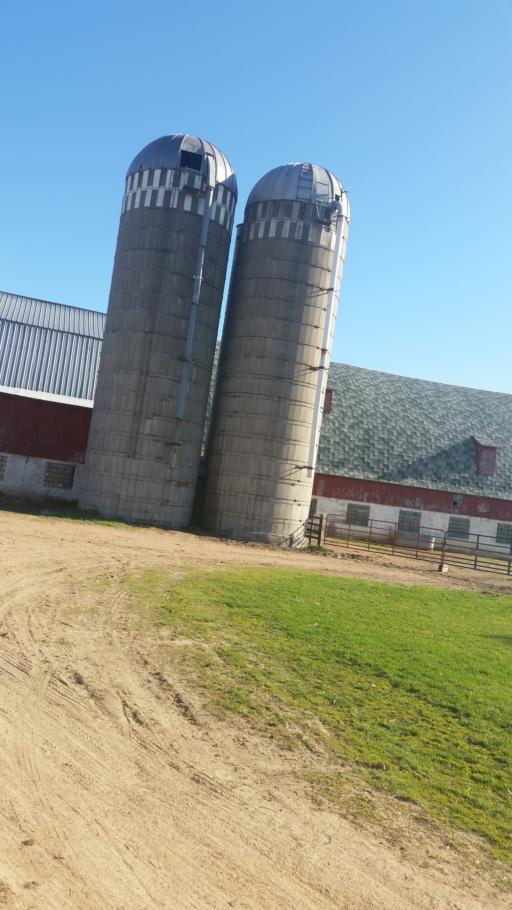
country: US
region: Wisconsin
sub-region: Clark County
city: Loyal
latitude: 44.6692
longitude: -90.4320
